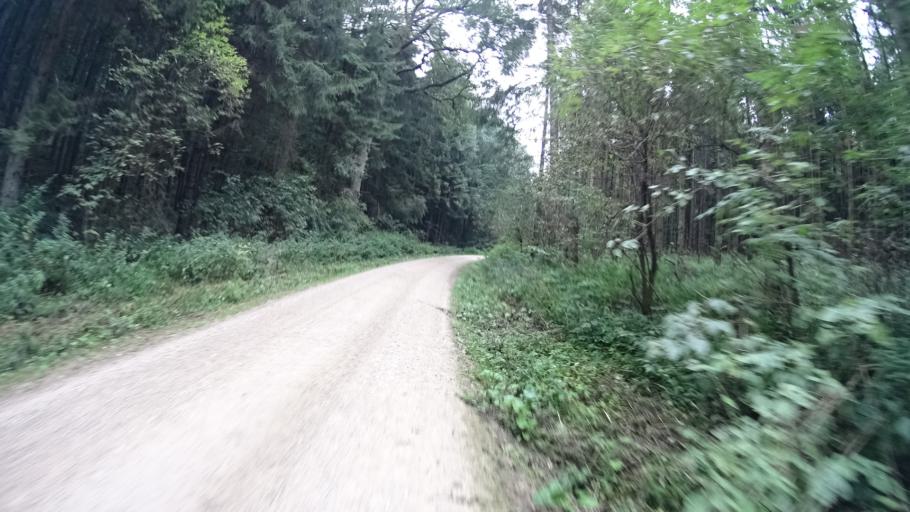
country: DE
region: Bavaria
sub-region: Upper Bavaria
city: Stammham
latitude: 48.8488
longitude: 11.4870
